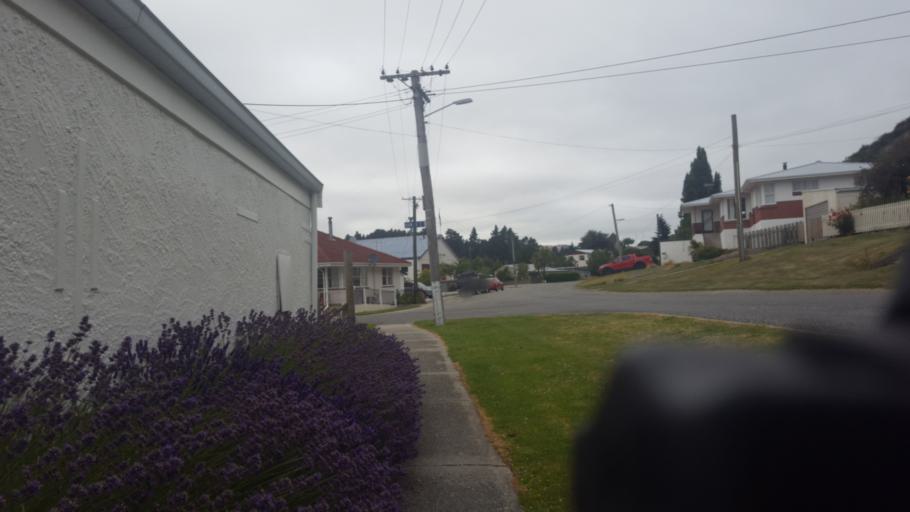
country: NZ
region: Otago
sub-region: Queenstown-Lakes District
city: Kingston
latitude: -45.5407
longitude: 169.3131
